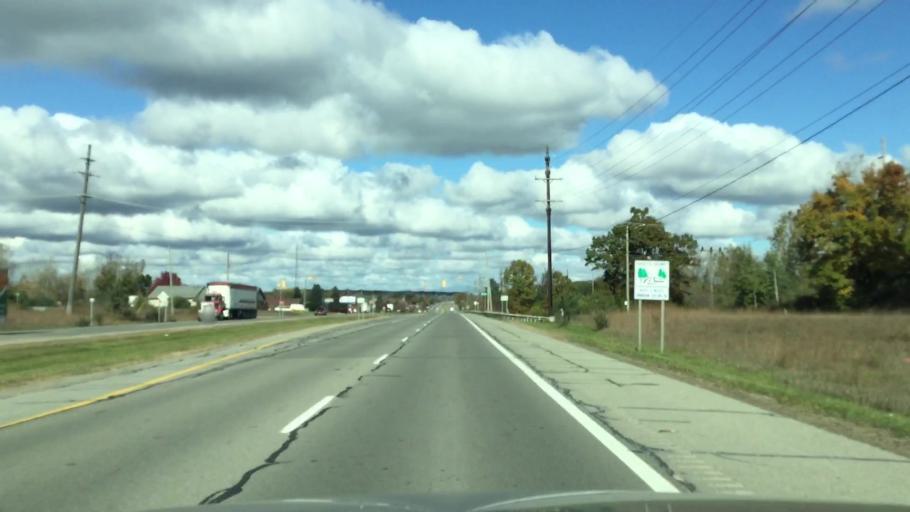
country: US
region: Michigan
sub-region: Oakland County
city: Oxford
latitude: 42.8480
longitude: -83.2793
